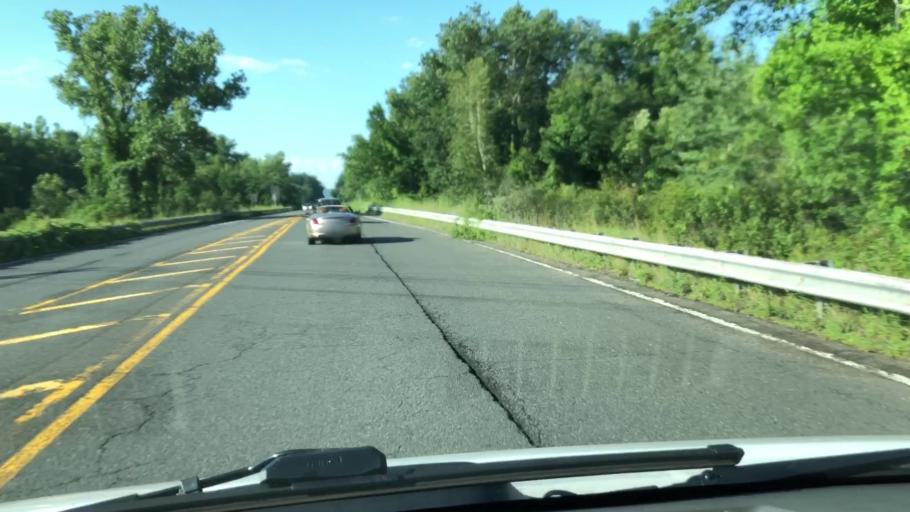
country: US
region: Massachusetts
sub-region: Hampshire County
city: North Amherst
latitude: 42.4080
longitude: -72.5381
